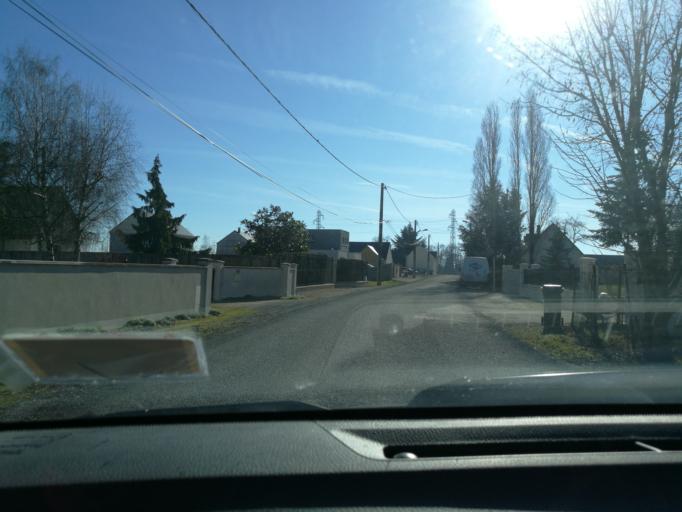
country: FR
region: Centre
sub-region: Departement du Loiret
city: Mareau-aux-Pres
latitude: 47.8805
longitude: 1.7869
